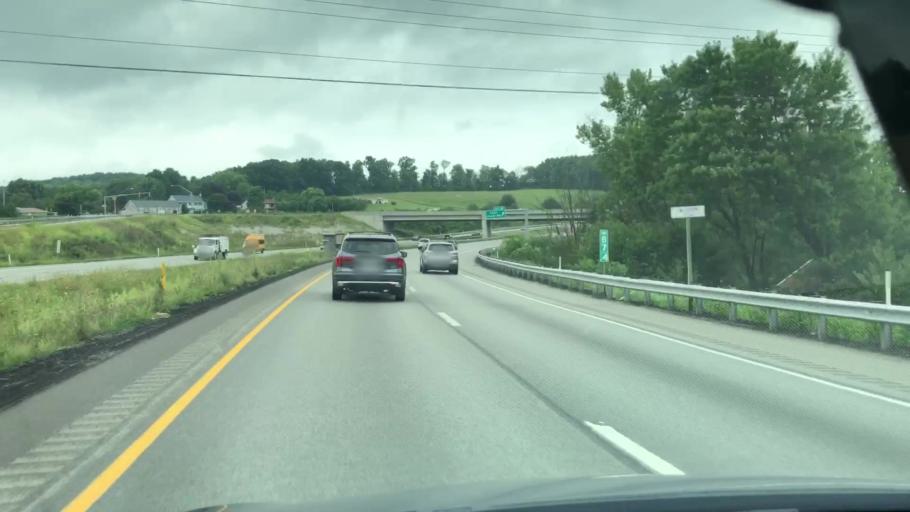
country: US
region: Pennsylvania
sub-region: Butler County
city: Zelienople
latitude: 40.8087
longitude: -80.1171
